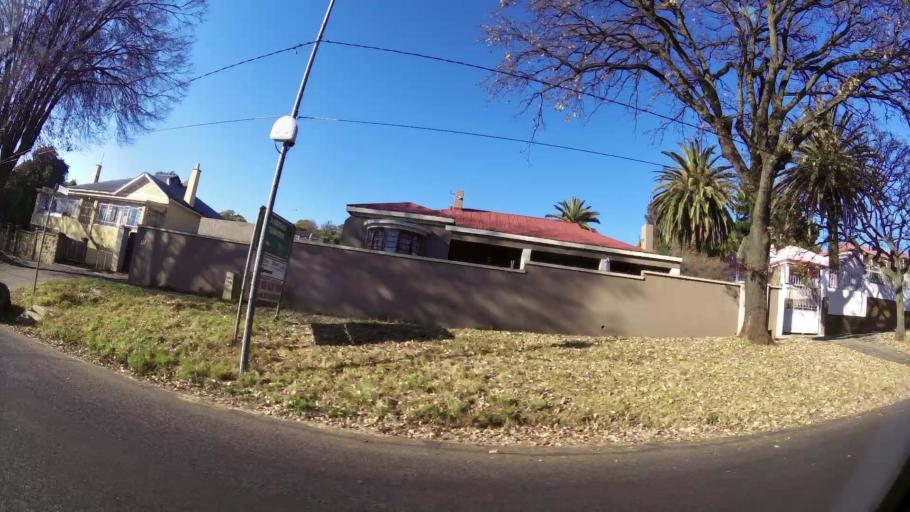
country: ZA
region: Gauteng
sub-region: City of Johannesburg Metropolitan Municipality
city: Johannesburg
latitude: -26.1981
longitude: 28.0874
